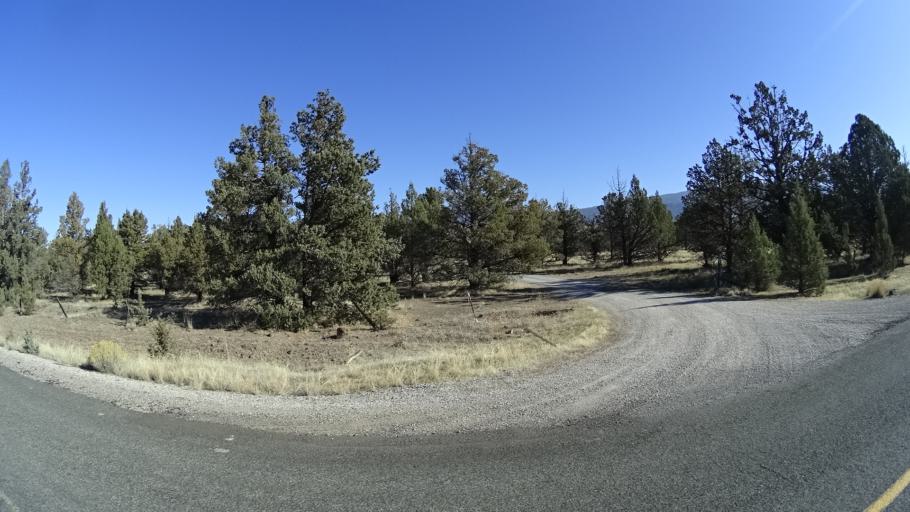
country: US
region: California
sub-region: Siskiyou County
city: Montague
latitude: 41.6592
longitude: -122.3664
